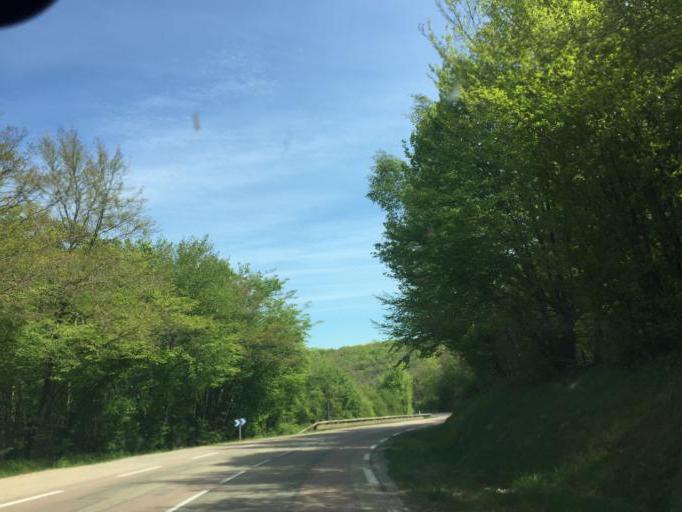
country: FR
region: Bourgogne
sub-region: Departement de l'Yonne
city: Avallon
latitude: 47.4550
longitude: 3.7119
